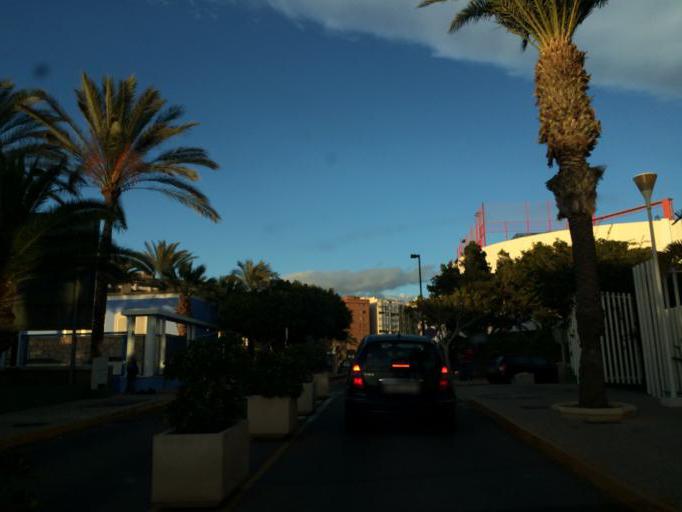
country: ES
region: Andalusia
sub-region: Provincia de Almeria
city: Almeria
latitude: 36.8318
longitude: -2.4609
